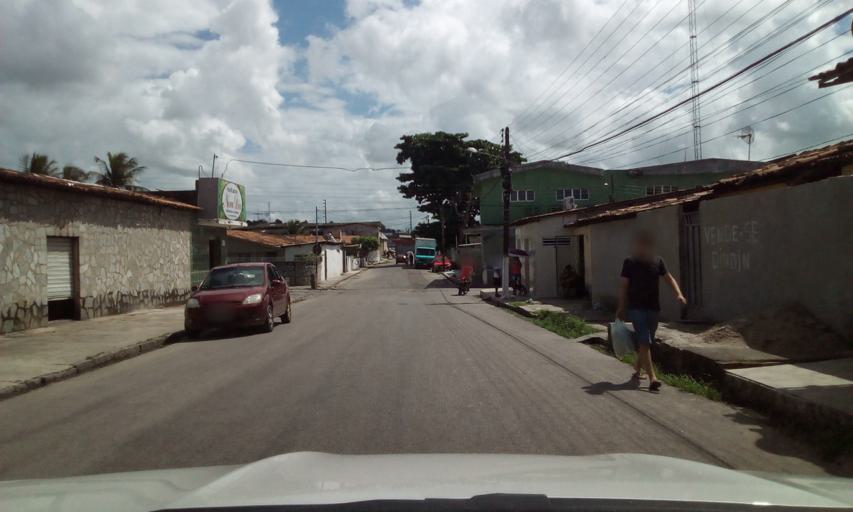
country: BR
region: Paraiba
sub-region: Bayeux
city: Bayeux
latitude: -7.1336
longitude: -34.9276
